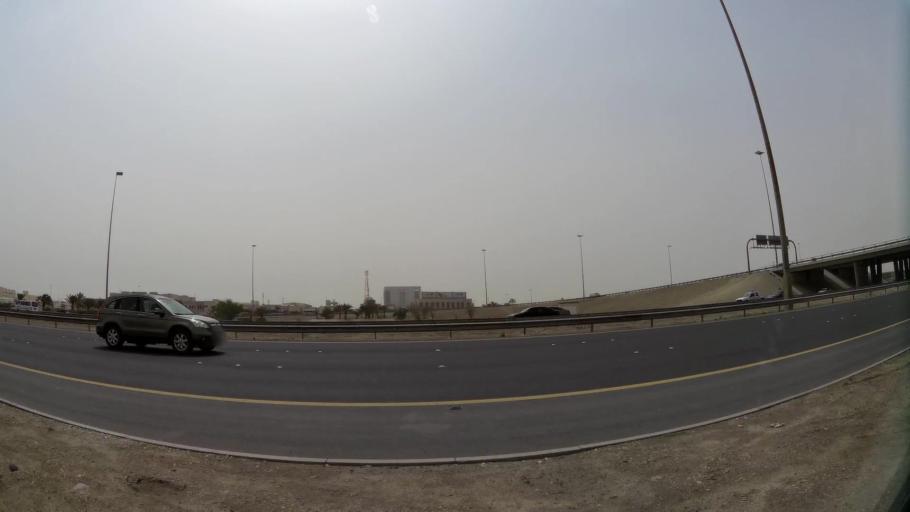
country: BH
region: Northern
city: Madinat `Isa
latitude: 26.1958
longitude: 50.5358
